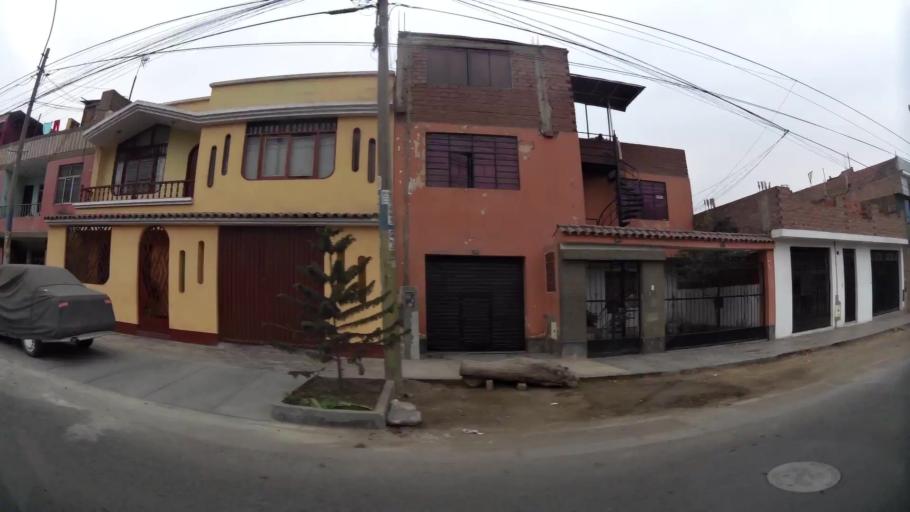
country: PE
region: Lima
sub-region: Lima
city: Independencia
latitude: -11.9847
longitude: -77.0117
